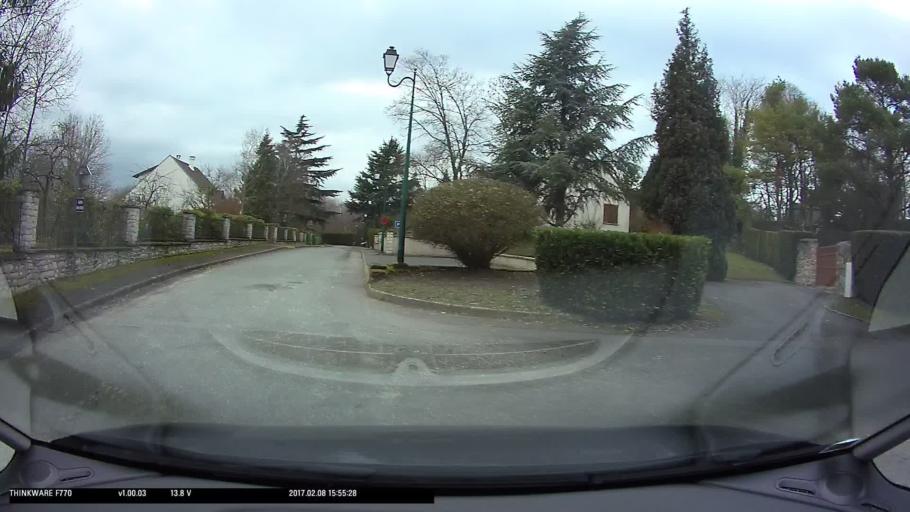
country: FR
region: Ile-de-France
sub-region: Departement du Val-d'Oise
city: Vigny
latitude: 49.0770
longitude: 1.9372
